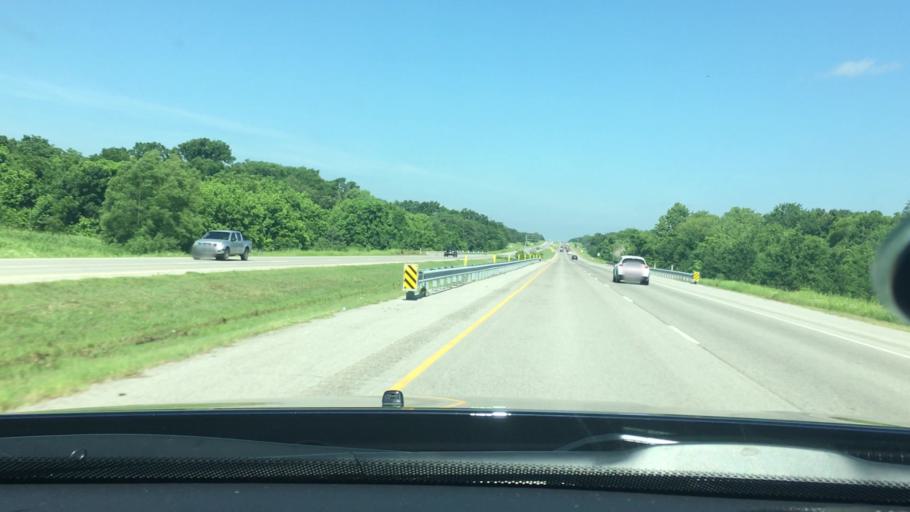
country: US
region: Oklahoma
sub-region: Carter County
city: Ardmore
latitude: 34.1345
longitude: -97.1010
